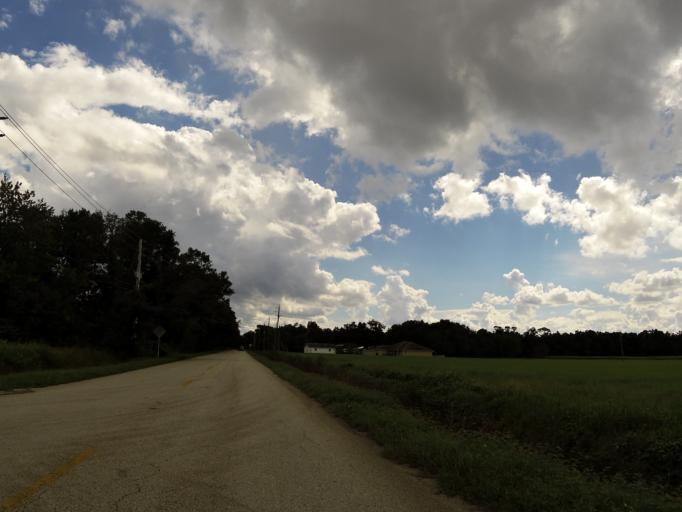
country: US
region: Florida
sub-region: Saint Johns County
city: Saint Augustine South
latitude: 29.8426
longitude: -81.4996
